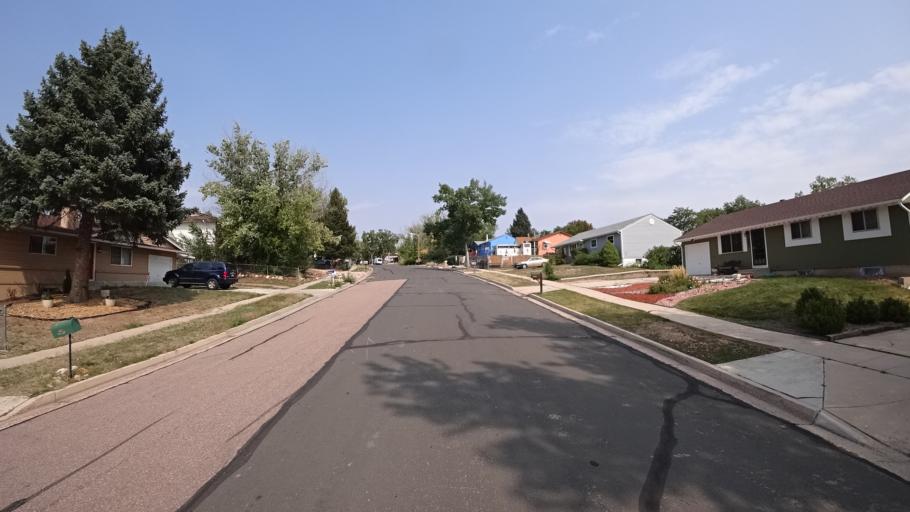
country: US
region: Colorado
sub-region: El Paso County
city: Cimarron Hills
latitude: 38.8313
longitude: -104.7529
